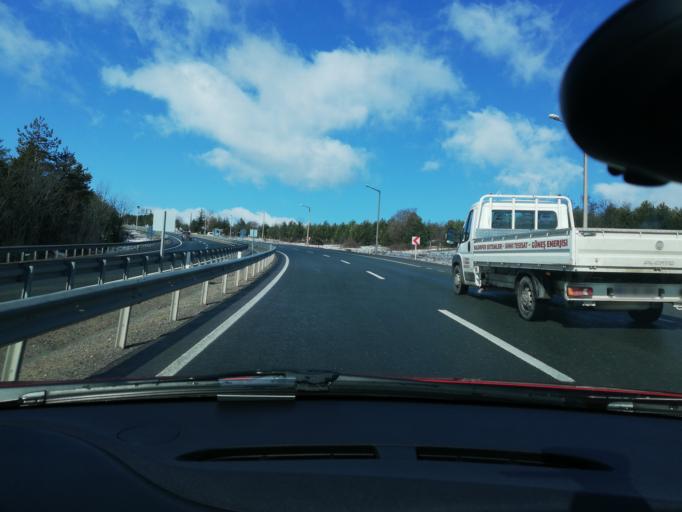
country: TR
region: Kastamonu
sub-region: Cide
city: Kastamonu
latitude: 41.3685
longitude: 33.7567
